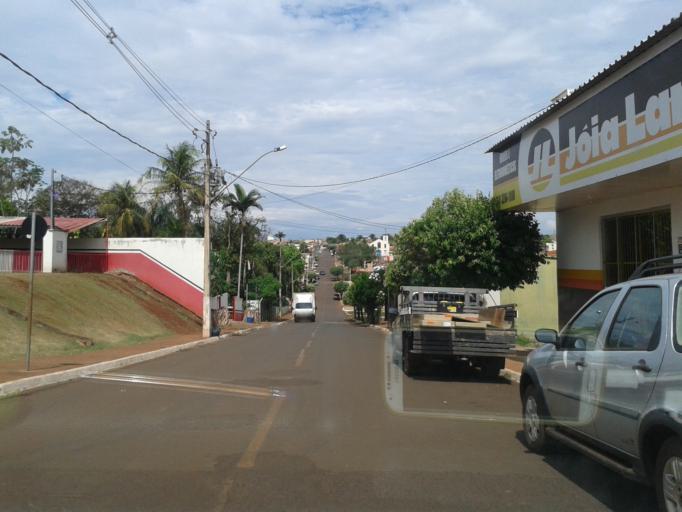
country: BR
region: Goias
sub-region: Itumbiara
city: Itumbiara
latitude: -18.4353
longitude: -49.1880
